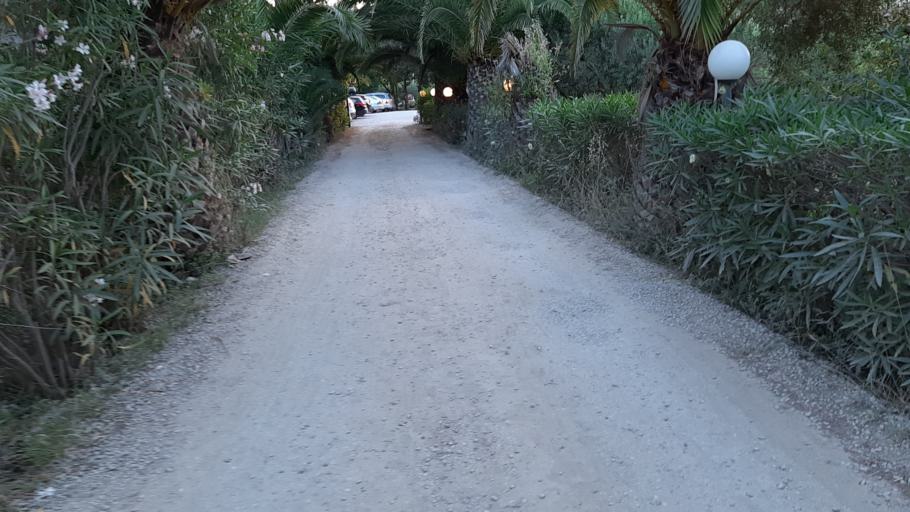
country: IT
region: Tuscany
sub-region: Provincia di Livorno
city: Portoferraio
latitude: 42.7595
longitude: 10.3125
